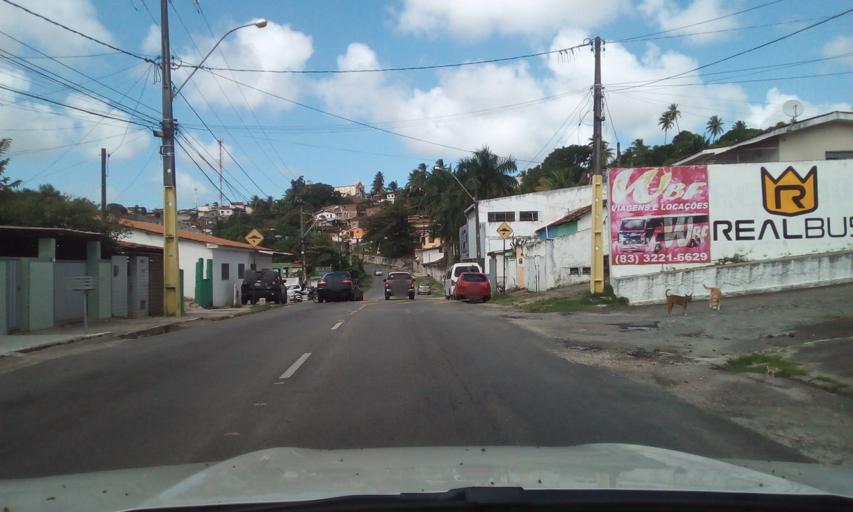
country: BR
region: Paraiba
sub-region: Joao Pessoa
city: Joao Pessoa
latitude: -7.1127
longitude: -34.8848
